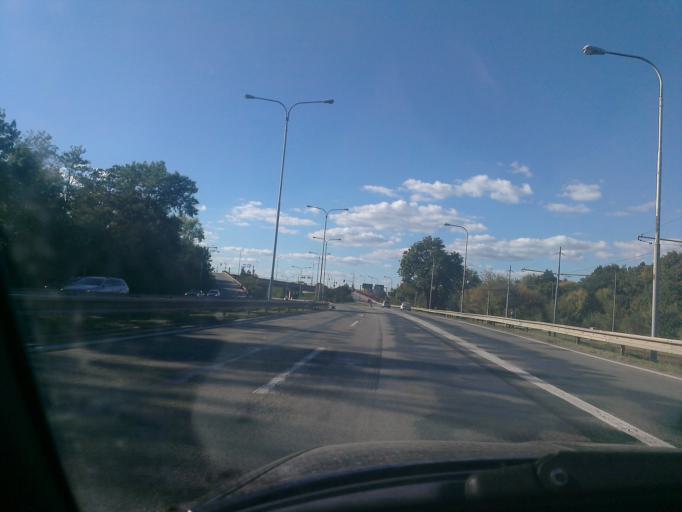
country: CZ
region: South Moravian
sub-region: Mesto Brno
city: Brno
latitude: 49.1892
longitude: 16.6525
